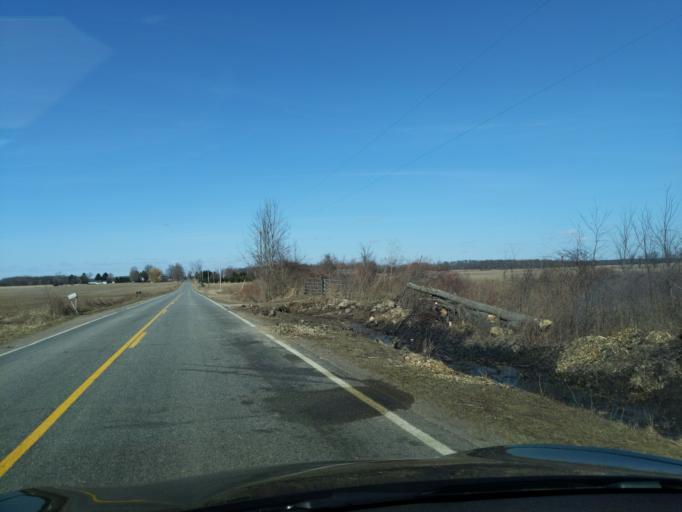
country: US
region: Michigan
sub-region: Ionia County
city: Saranac
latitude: 42.8936
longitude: -85.1342
